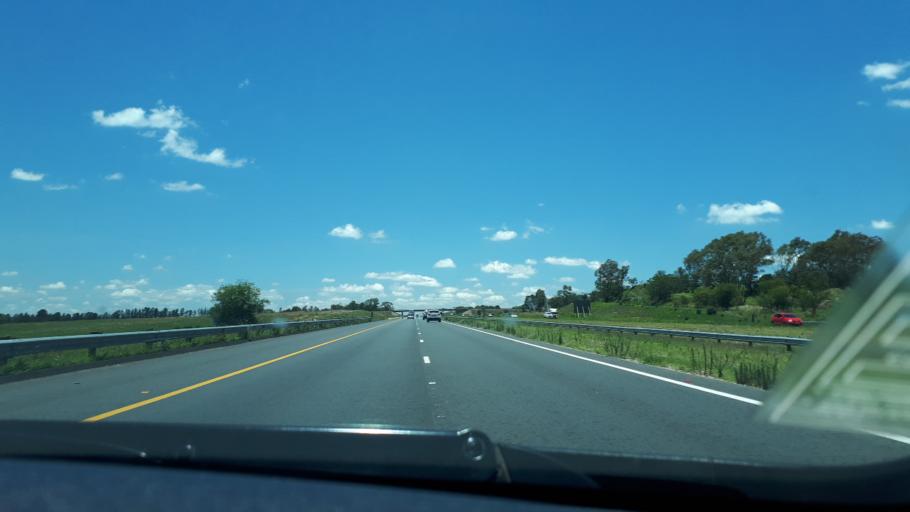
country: ZA
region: Gauteng
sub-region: City of Johannesburg Metropolitan Municipality
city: Diepsloot
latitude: -25.9758
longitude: 27.9362
